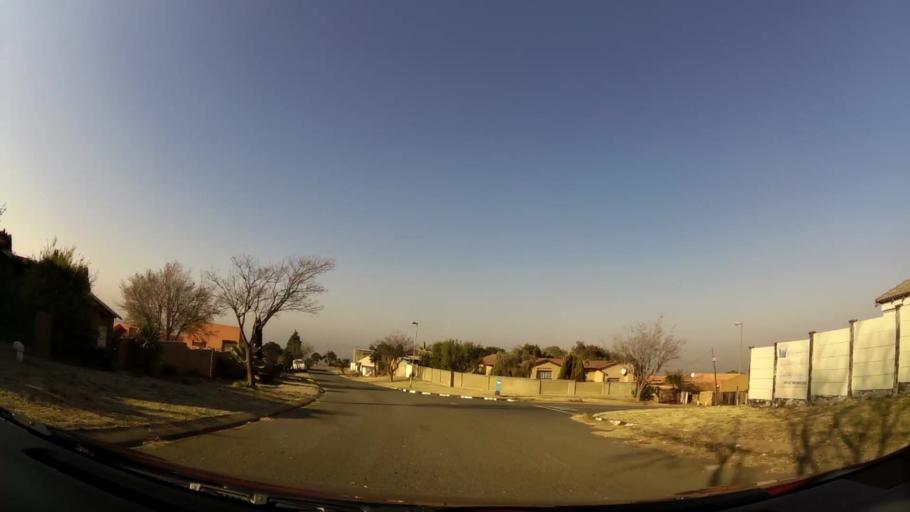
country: ZA
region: Gauteng
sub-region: City of Johannesburg Metropolitan Municipality
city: Soweto
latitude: -26.2890
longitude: 27.9571
